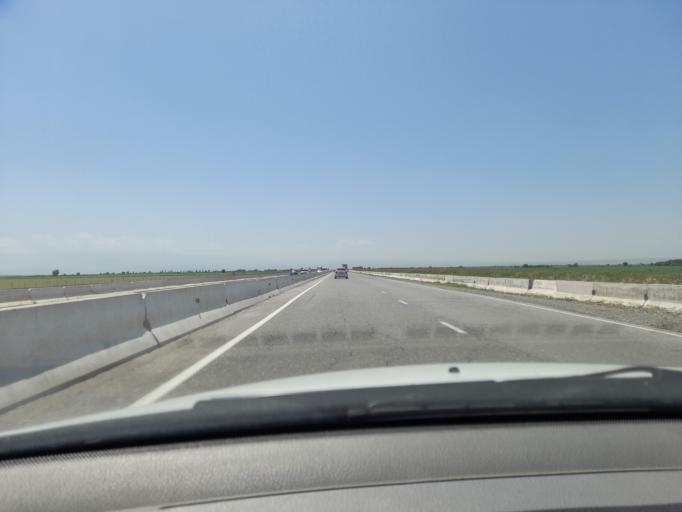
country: UZ
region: Jizzax
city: Paxtakor
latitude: 40.2312
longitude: 67.9995
